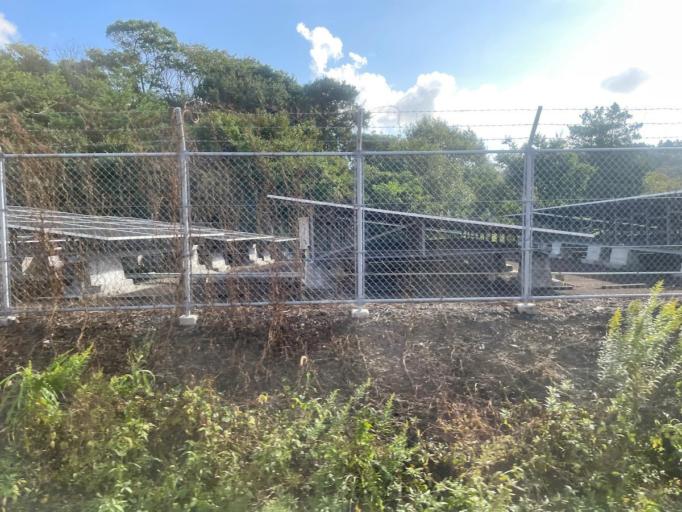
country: JP
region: Mie
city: Toba
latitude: 34.3432
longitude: 136.8164
